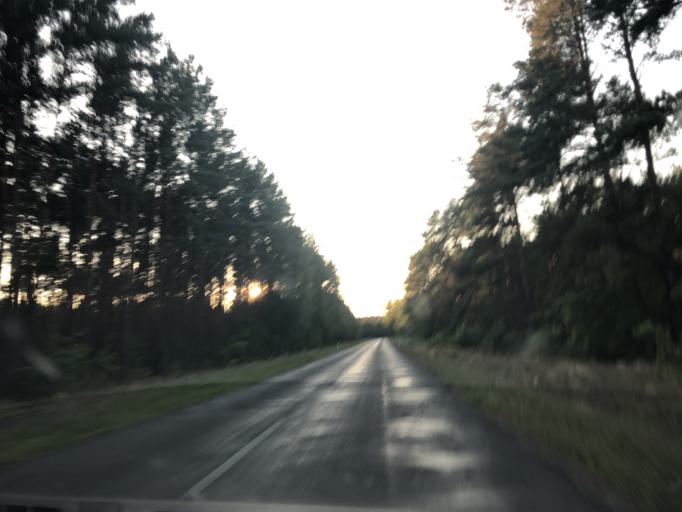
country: DE
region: Brandenburg
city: Mullrose
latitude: 52.2470
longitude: 14.4702
